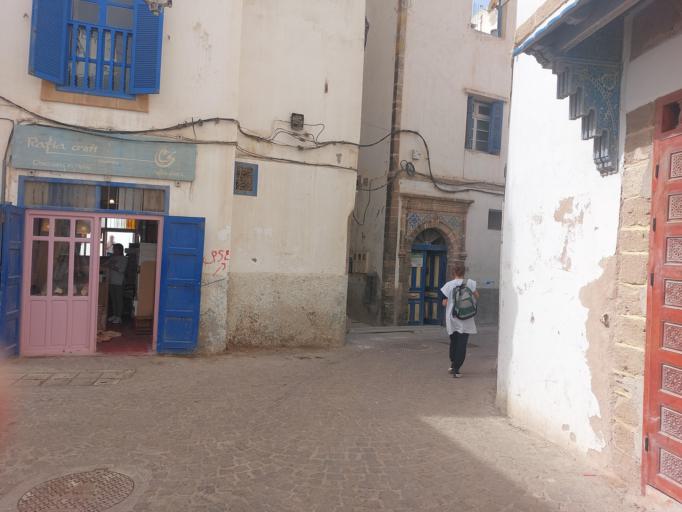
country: MA
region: Marrakech-Tensift-Al Haouz
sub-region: Essaouira
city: Essaouira
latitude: 31.5121
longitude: -9.7664
